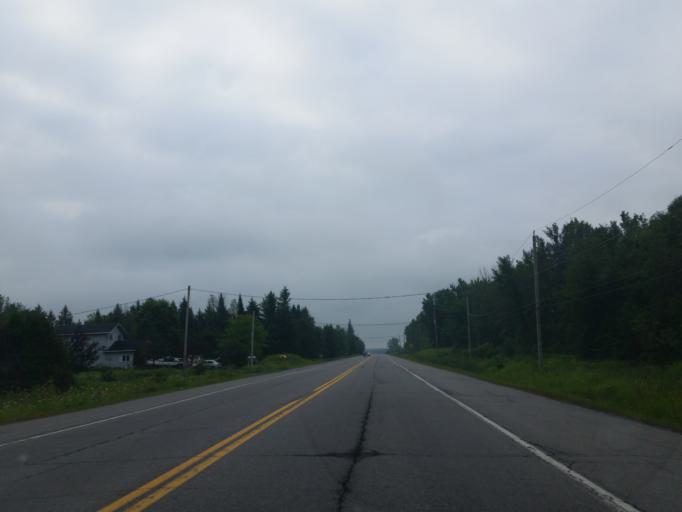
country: CA
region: Ontario
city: Clarence-Rockland
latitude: 45.4199
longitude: -75.4071
